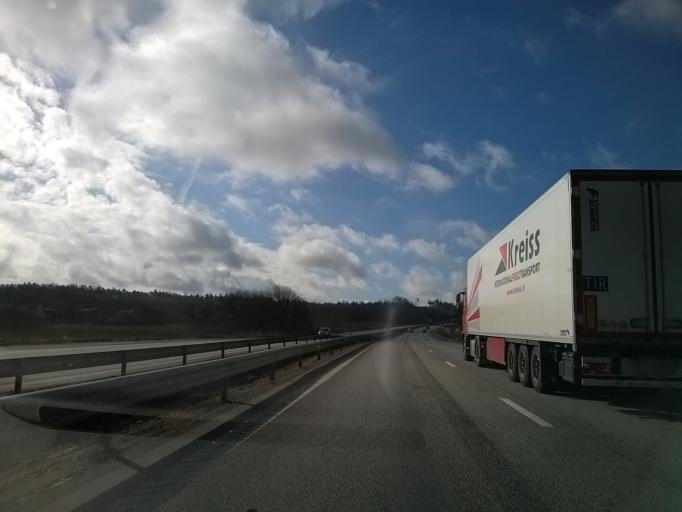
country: SE
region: Halland
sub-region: Kungsbacka Kommun
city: Kungsbacka
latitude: 57.5051
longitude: 12.0527
